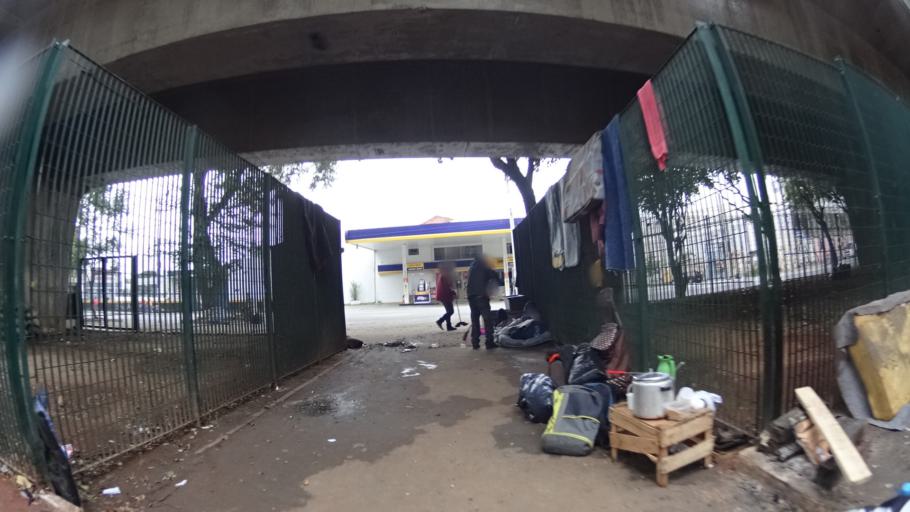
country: BR
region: Sao Paulo
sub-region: Sao Paulo
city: Sao Paulo
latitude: -23.5262
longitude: -46.6303
